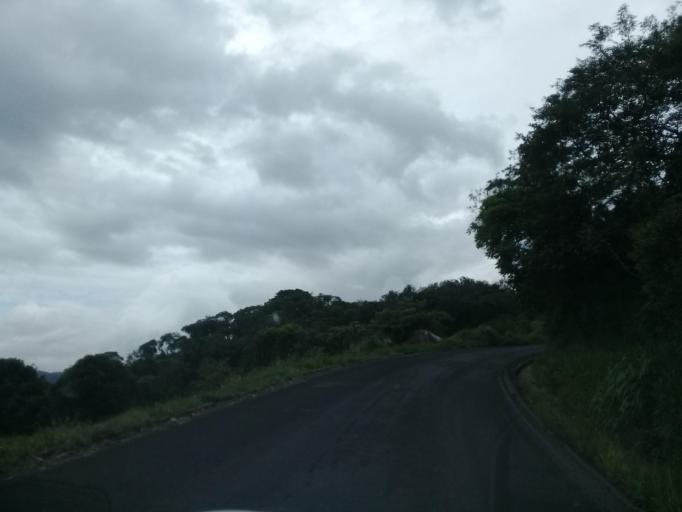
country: MX
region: Veracruz
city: El Castillo
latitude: 19.5625
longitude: -96.8430
